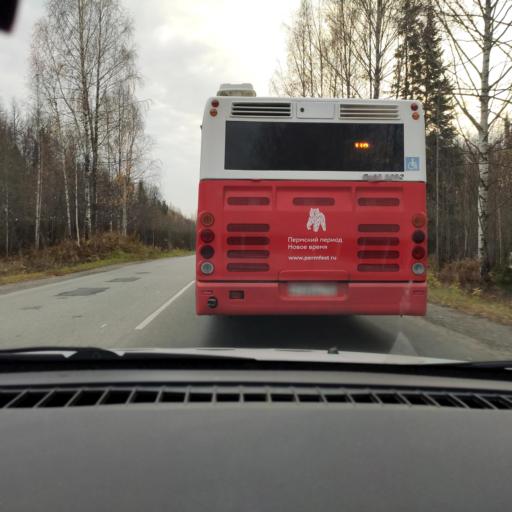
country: RU
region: Perm
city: Polazna
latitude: 58.1077
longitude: 56.4202
